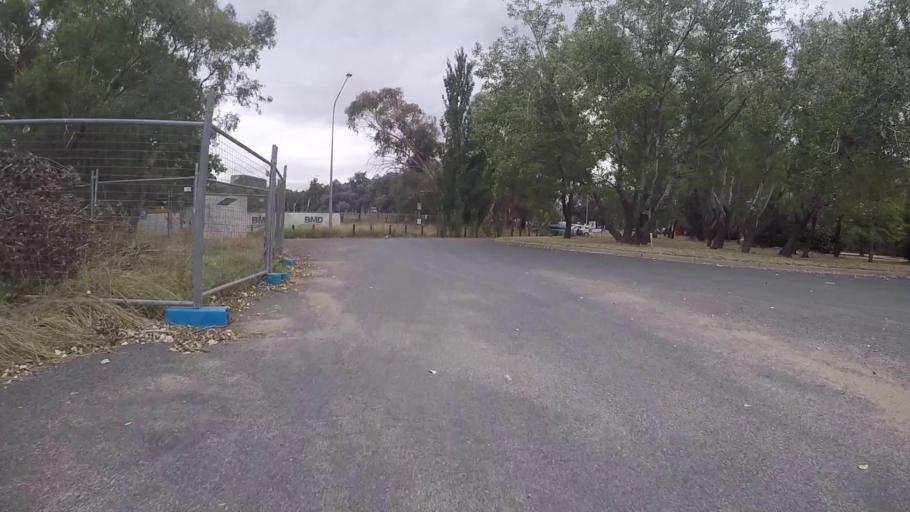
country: AU
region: Australian Capital Territory
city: Forrest
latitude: -35.3040
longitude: 149.1505
